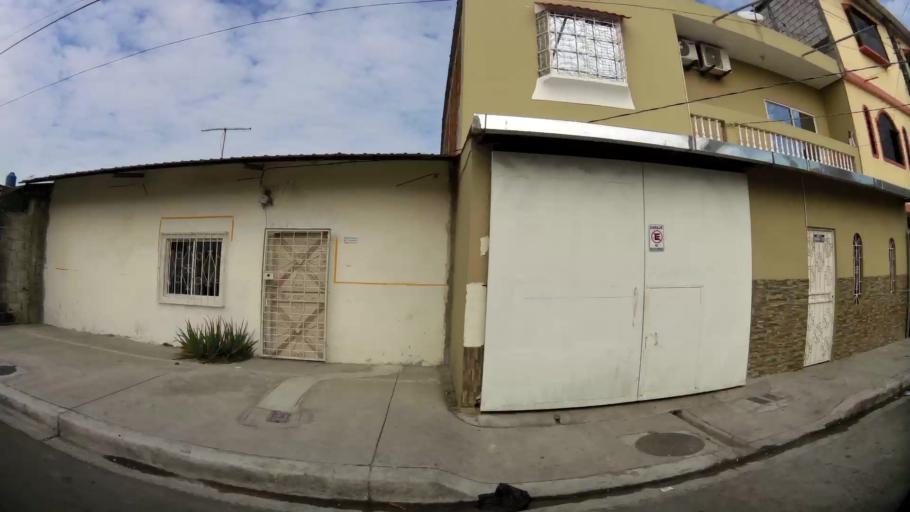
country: EC
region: Guayas
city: Guayaquil
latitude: -2.2495
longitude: -79.8808
